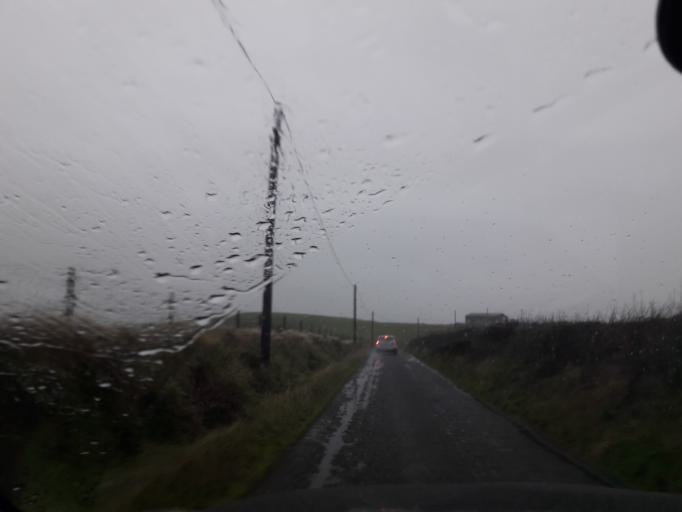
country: IE
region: Ulster
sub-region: County Donegal
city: Ramelton
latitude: 55.2652
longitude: -7.6454
